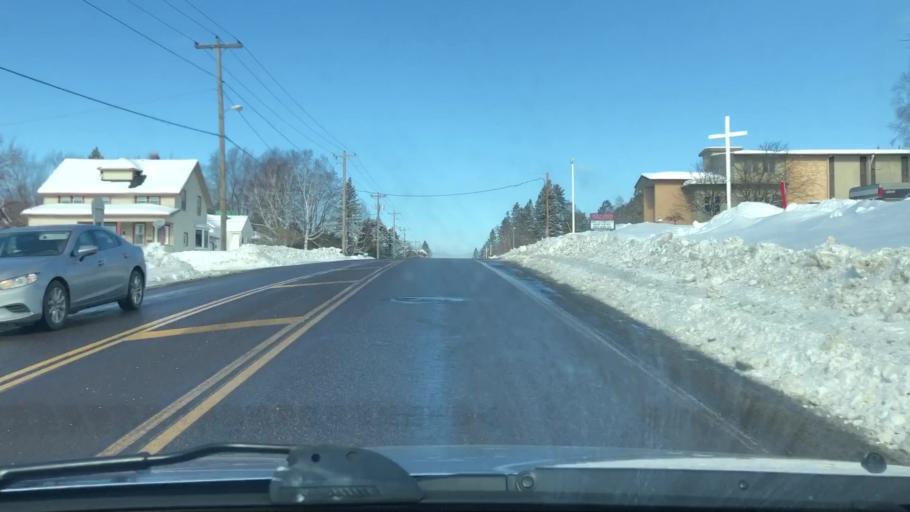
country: US
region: Minnesota
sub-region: Saint Louis County
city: Duluth
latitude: 46.8018
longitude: -92.1322
